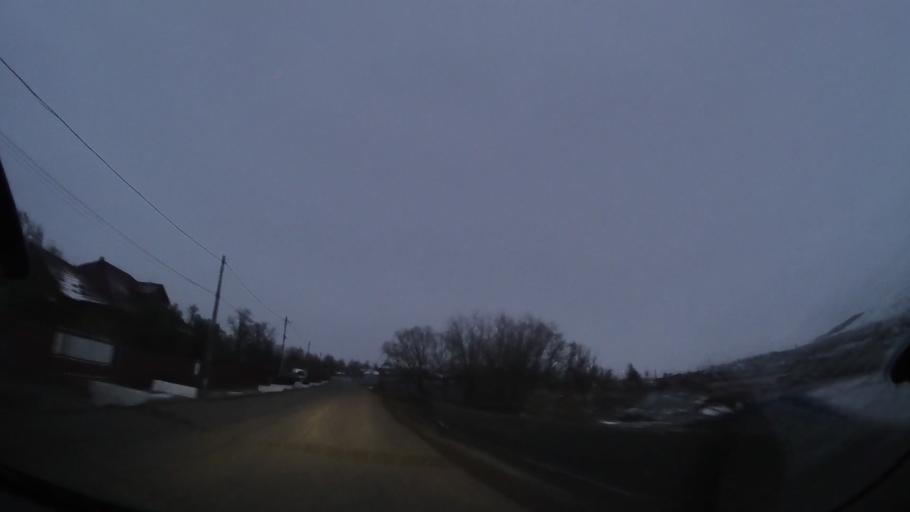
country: RO
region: Vaslui
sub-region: Comuna Vutcani
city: Vutcani
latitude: 46.4544
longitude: 28.0220
